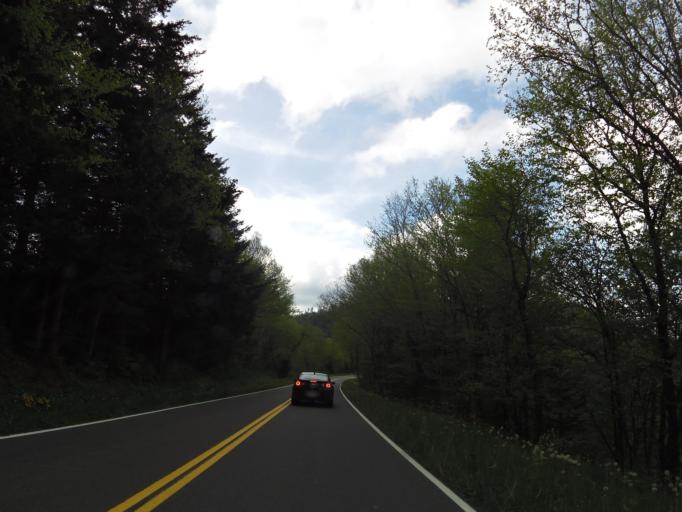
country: US
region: Tennessee
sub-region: Sevier County
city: Gatlinburg
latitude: 35.5755
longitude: -83.4809
